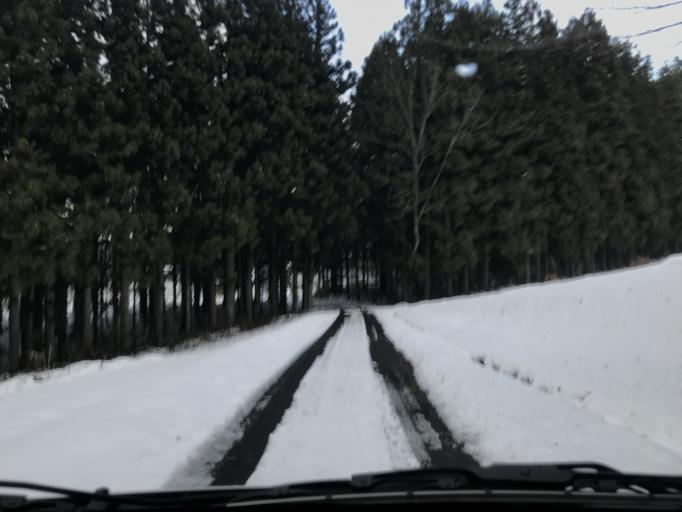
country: JP
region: Iwate
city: Mizusawa
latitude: 39.0501
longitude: 141.0508
